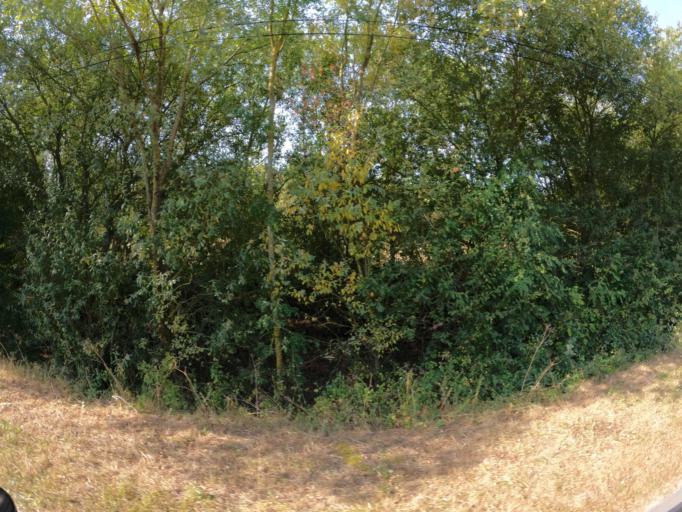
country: FR
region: Pays de la Loire
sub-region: Departement de la Vendee
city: Le Perrier
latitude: 46.8034
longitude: -1.9654
